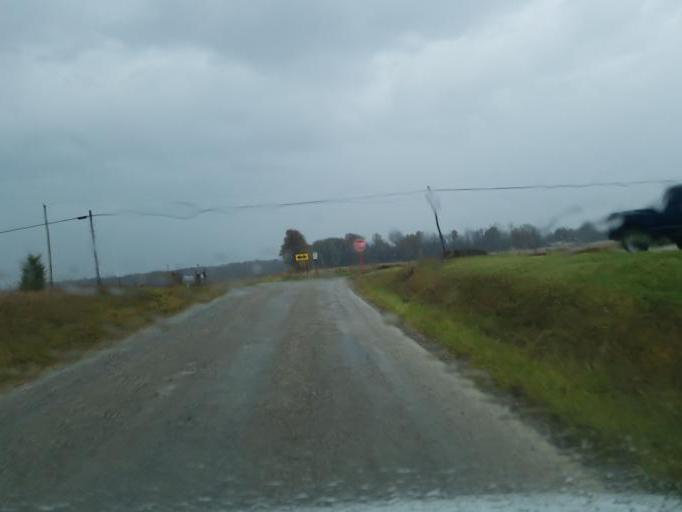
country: US
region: Ohio
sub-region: Morrow County
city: Cardington
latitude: 40.4668
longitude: -82.8804
